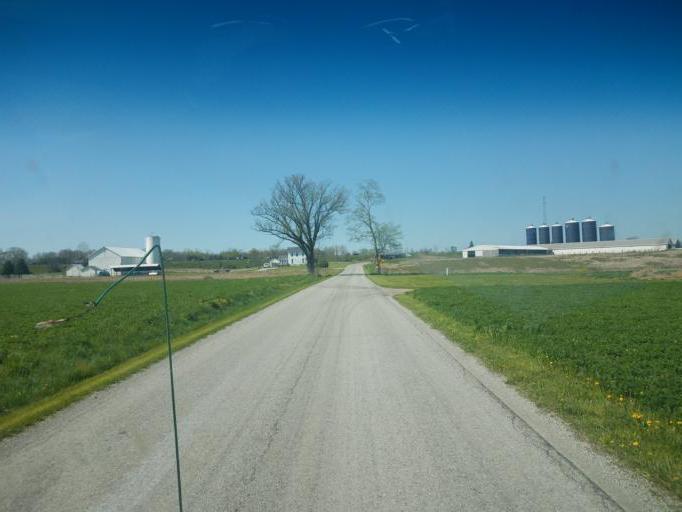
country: US
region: Ohio
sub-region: Medina County
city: Lodi
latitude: 40.9828
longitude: -82.0354
